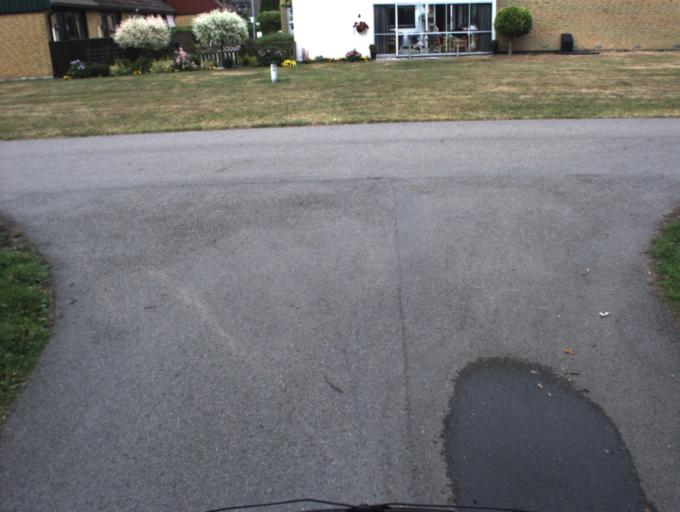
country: SE
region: Skane
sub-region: Helsingborg
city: Helsingborg
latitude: 56.0297
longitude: 12.7460
